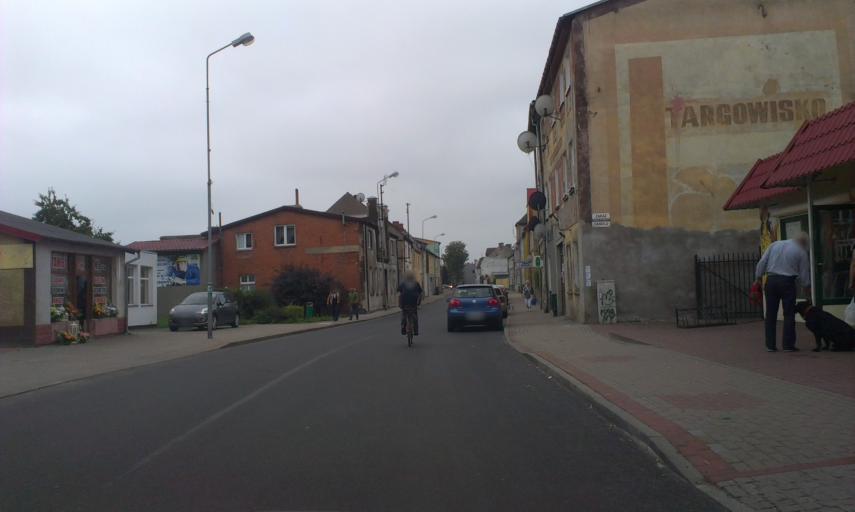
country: PL
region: West Pomeranian Voivodeship
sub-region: Powiat szczecinecki
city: Barwice
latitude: 53.7427
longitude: 16.3555
